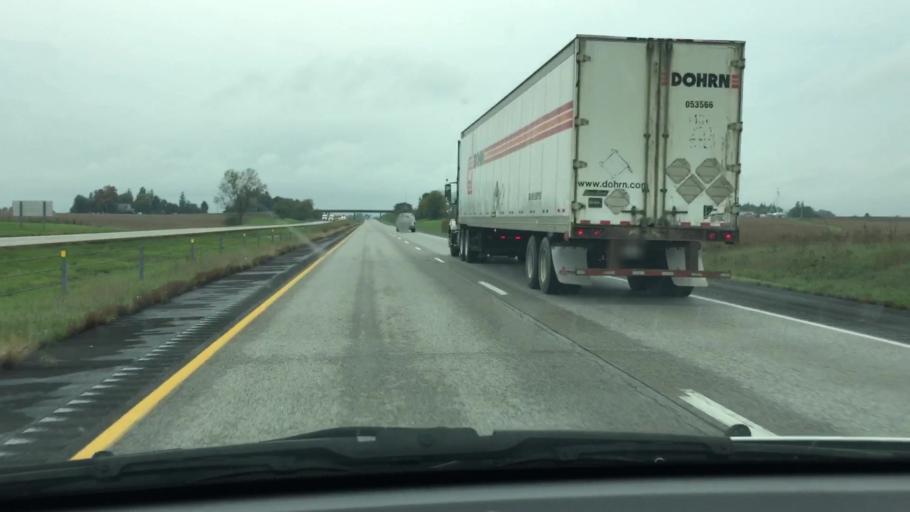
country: US
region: Iowa
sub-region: Johnson County
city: Tiffin
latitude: 41.6935
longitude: -91.7471
